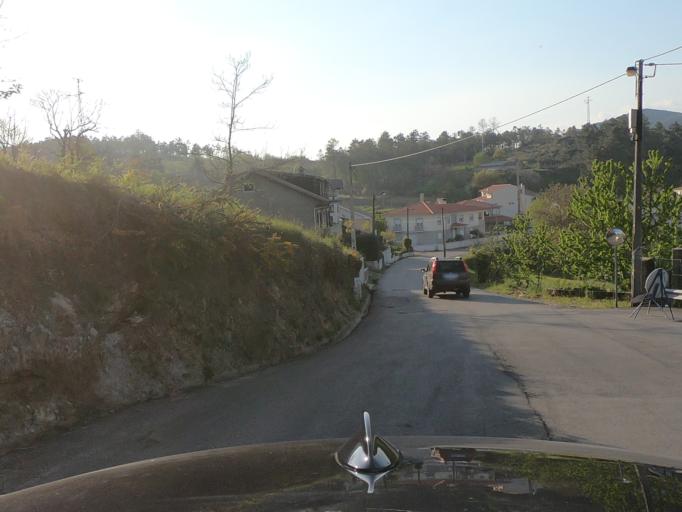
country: PT
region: Vila Real
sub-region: Santa Marta de Penaguiao
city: Santa Marta de Penaguiao
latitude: 41.2771
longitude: -7.8146
